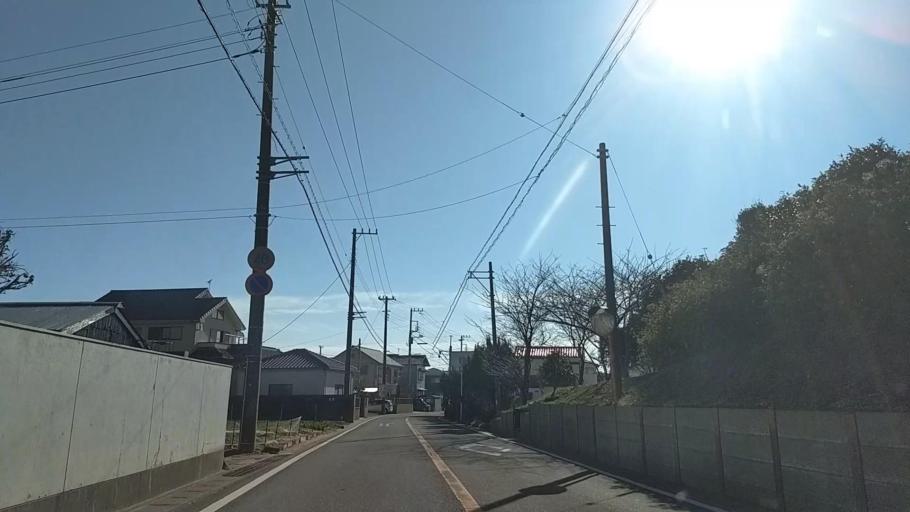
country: JP
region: Chiba
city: Hasaki
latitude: 35.7226
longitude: 140.8521
